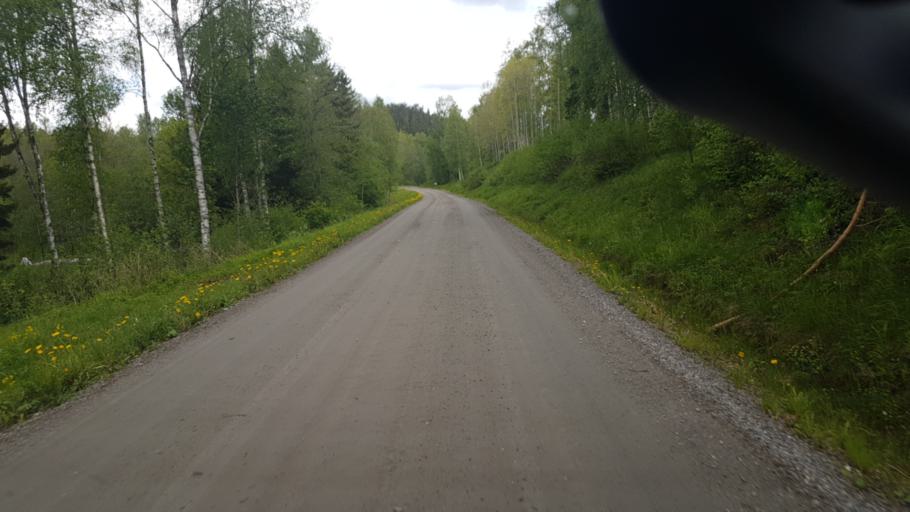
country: NO
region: Ostfold
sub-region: Romskog
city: Romskog
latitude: 59.6806
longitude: 11.9329
